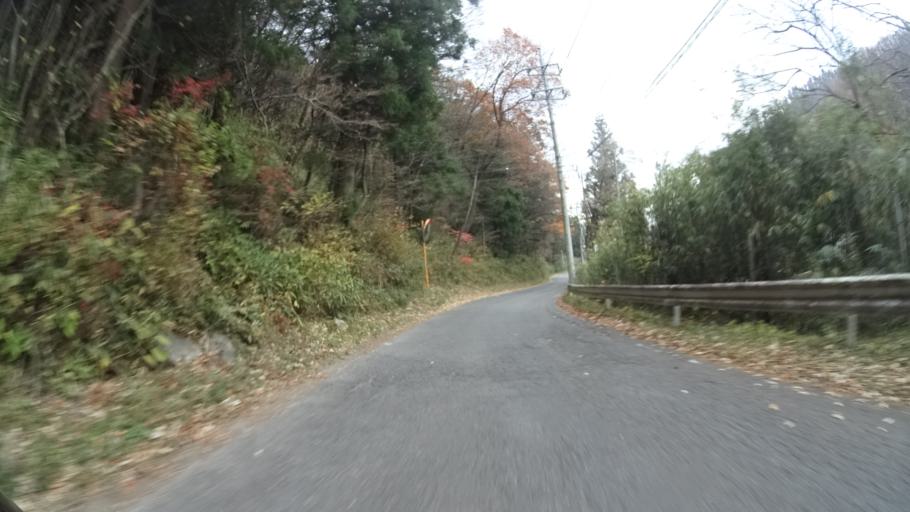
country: JP
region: Gunma
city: Omamacho-omama
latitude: 36.4911
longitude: 139.1850
